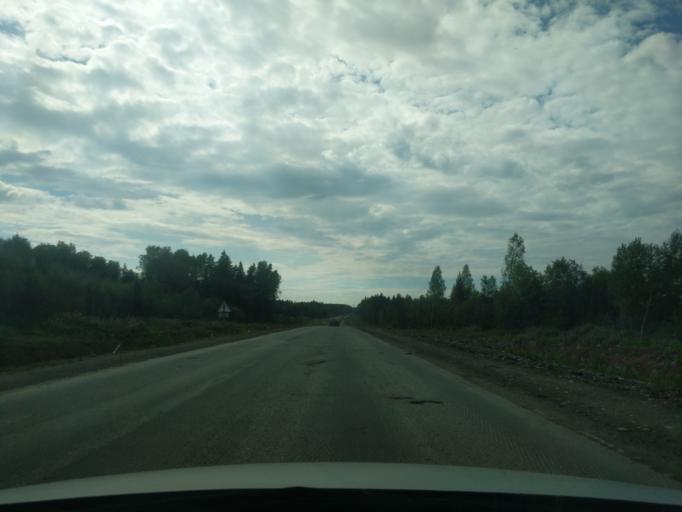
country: RU
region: Kostroma
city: Sudislavl'
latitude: 57.8546
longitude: 41.6024
